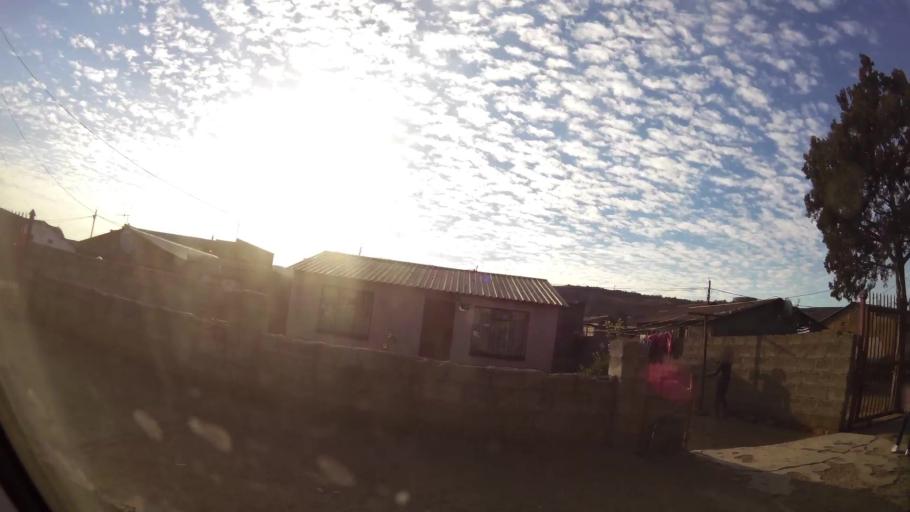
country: ZA
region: Gauteng
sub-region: City of Tshwane Metropolitan Municipality
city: Cullinan
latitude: -25.7085
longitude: 28.3835
